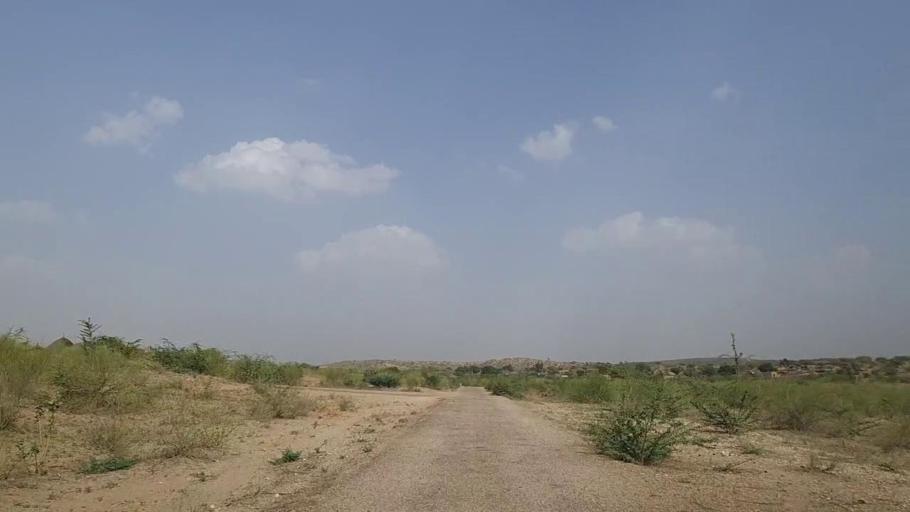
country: PK
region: Sindh
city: Islamkot
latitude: 24.8752
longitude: 70.1644
